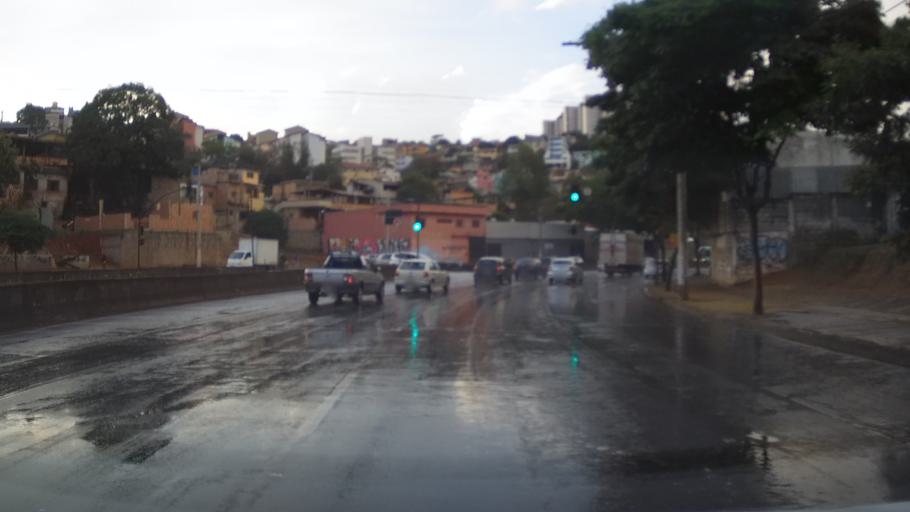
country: BR
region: Minas Gerais
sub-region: Belo Horizonte
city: Belo Horizonte
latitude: -19.9432
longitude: -43.9875
